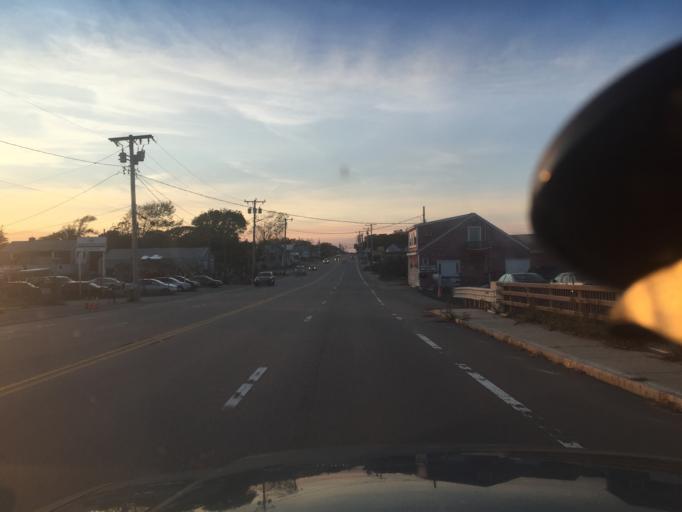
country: US
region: Massachusetts
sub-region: Barnstable County
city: Buzzards Bay
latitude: 41.7474
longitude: -70.6219
